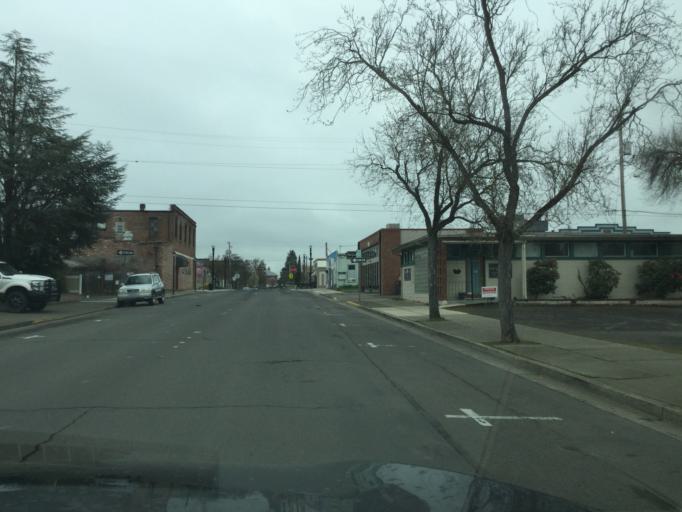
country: US
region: Oregon
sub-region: Jackson County
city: Central Point
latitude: 42.3760
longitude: -122.9162
